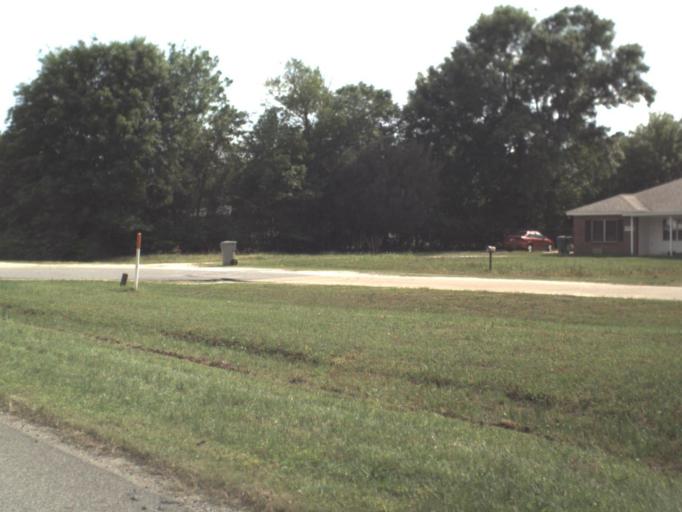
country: US
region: Florida
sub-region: Escambia County
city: Gonzalez
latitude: 30.5533
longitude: -87.2839
